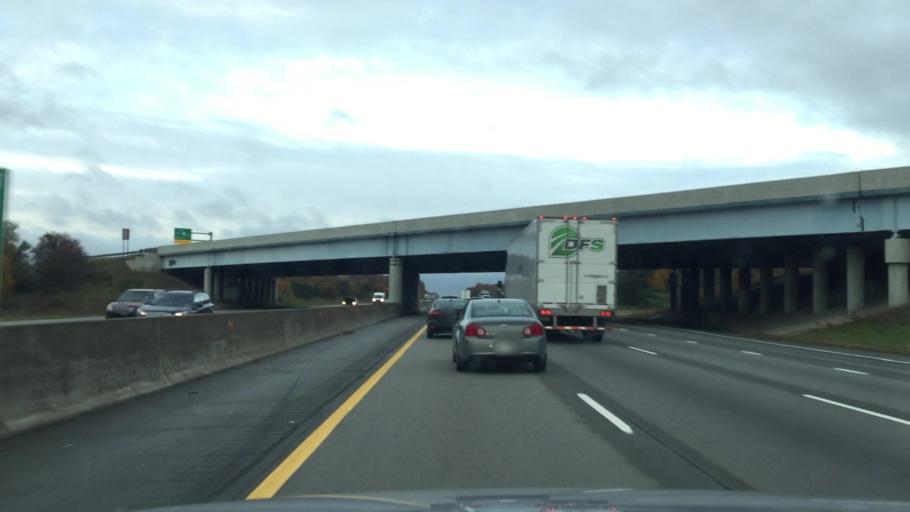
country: US
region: Michigan
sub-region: Washtenaw County
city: Ypsilanti
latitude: 42.2243
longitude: -83.6503
